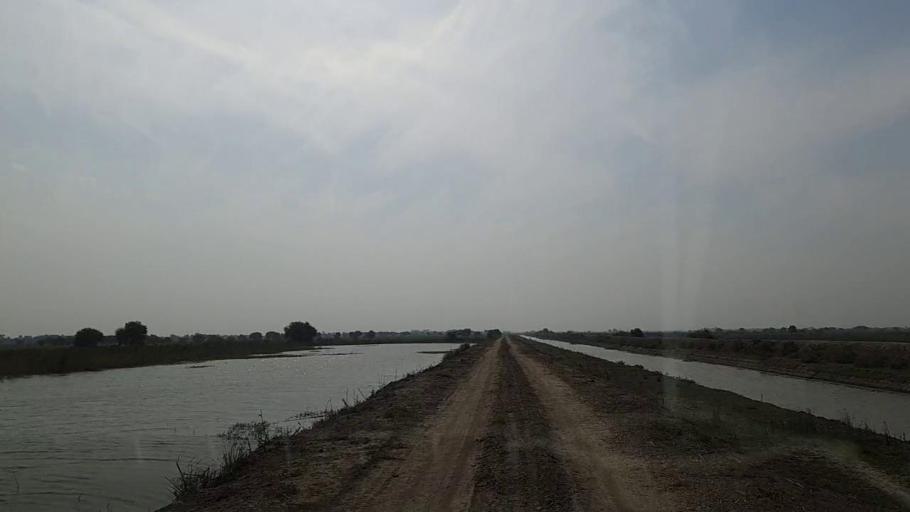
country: PK
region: Sindh
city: Mirpur Batoro
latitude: 24.6726
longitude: 68.2497
